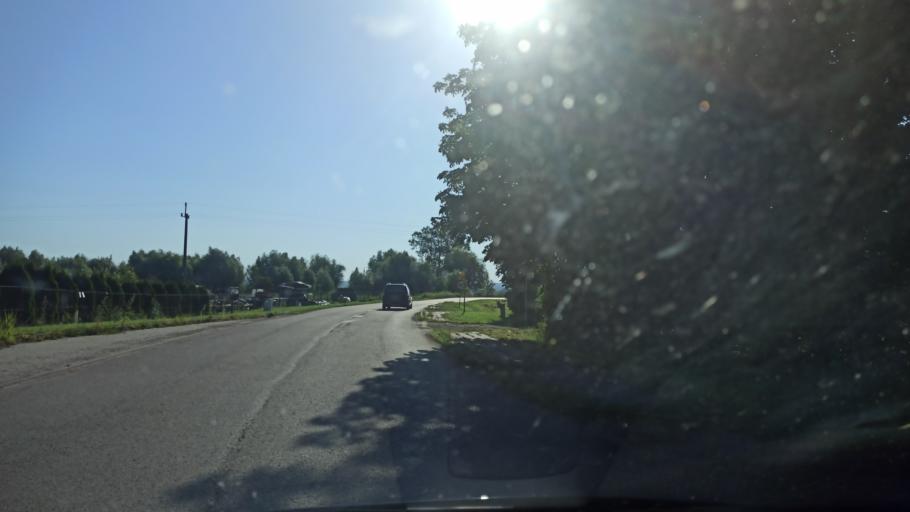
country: PL
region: Warmian-Masurian Voivodeship
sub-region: Powiat elblaski
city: Elblag
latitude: 54.1893
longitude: 19.3289
